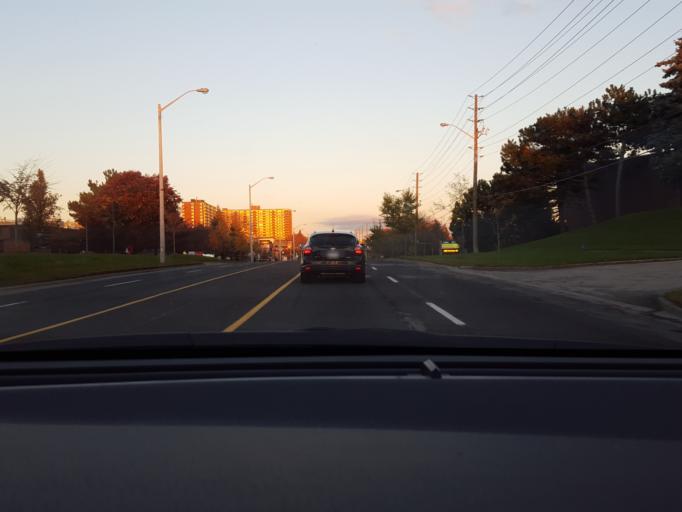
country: CA
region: Ontario
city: Scarborough
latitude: 43.7752
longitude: -79.2379
